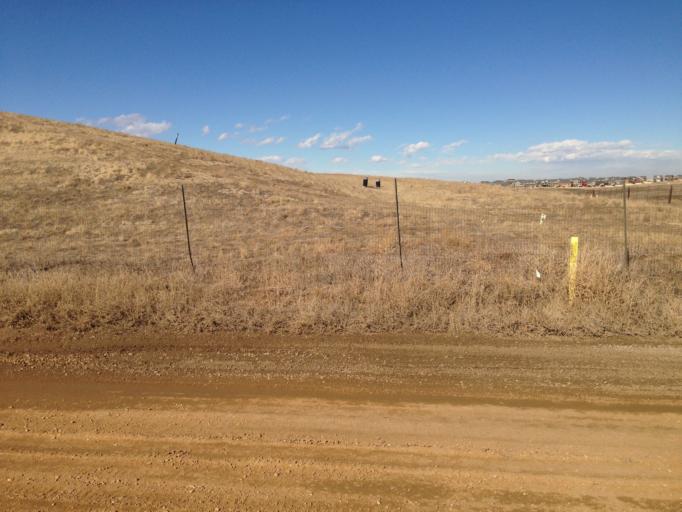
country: US
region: Colorado
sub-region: Boulder County
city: Erie
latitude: 40.0293
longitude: -105.0280
